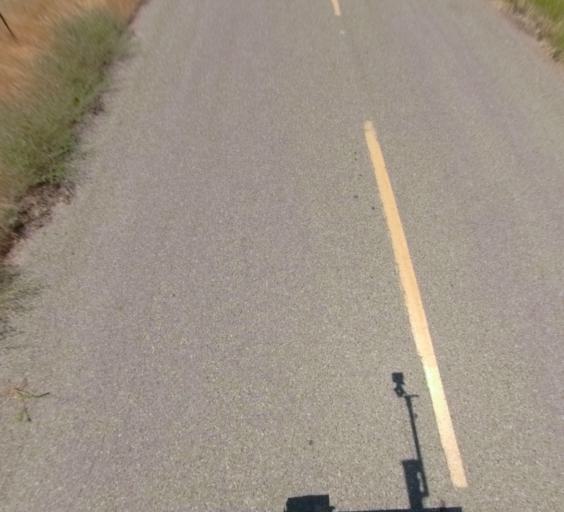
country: US
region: California
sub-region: Madera County
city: Madera Acres
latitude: 37.0912
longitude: -120.0100
